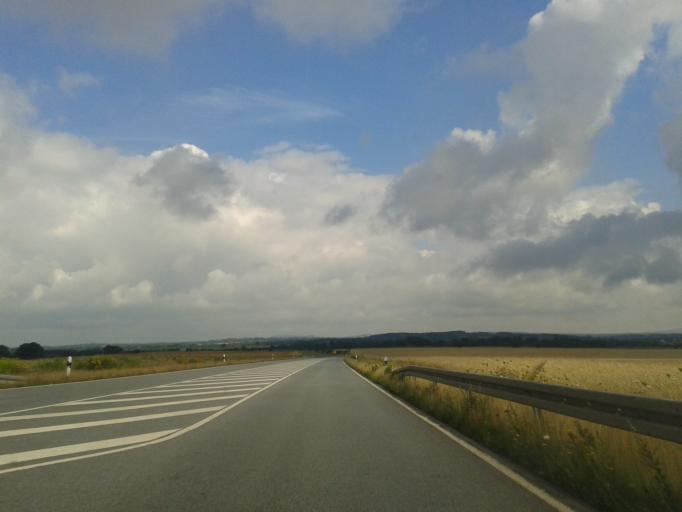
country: DE
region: Saxony
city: Radeberg
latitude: 51.0918
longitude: 13.9380
